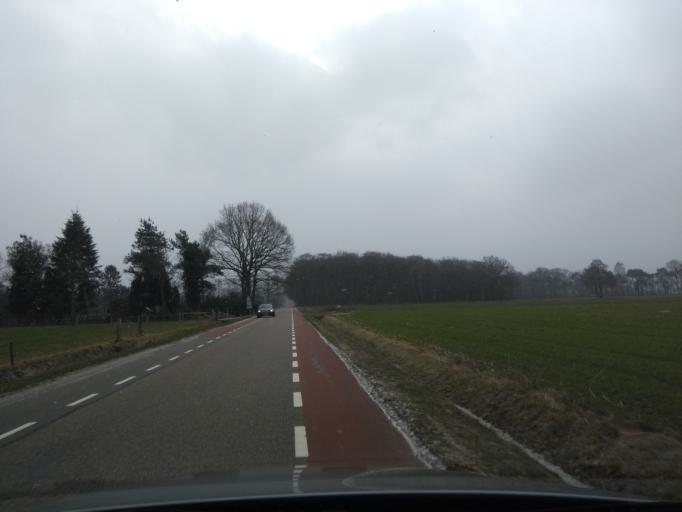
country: NL
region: Overijssel
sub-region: Gemeente Hof van Twente
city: Delden
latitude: 52.2256
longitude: 6.6949
